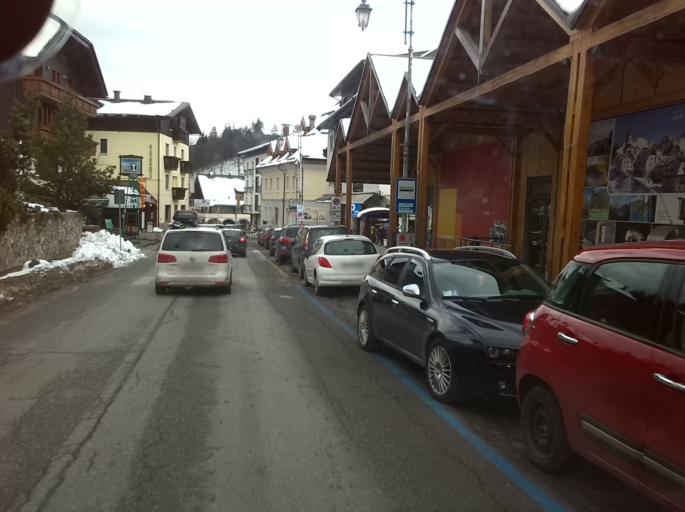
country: IT
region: Friuli Venezia Giulia
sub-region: Provincia di Udine
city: Tarvisio
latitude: 46.5042
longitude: 13.5819
